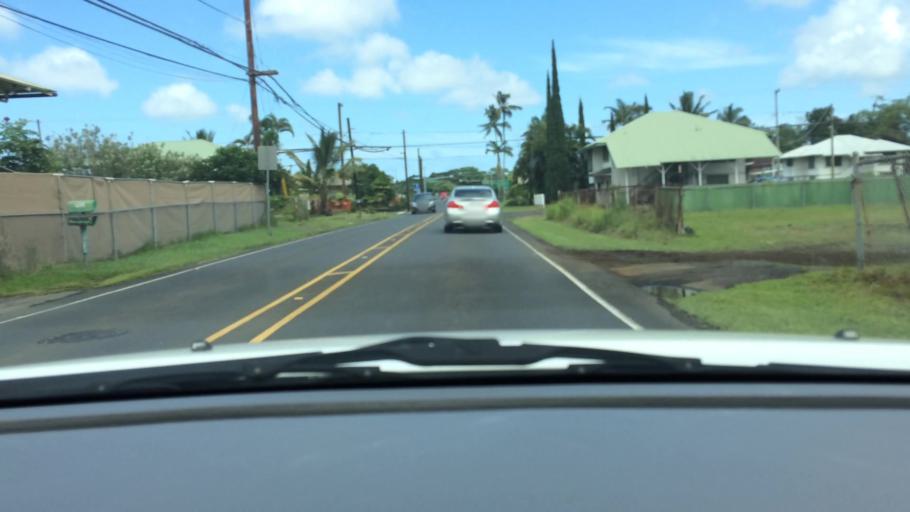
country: US
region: Hawaii
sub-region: Hawaii County
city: Hilo
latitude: 19.7117
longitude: -155.0666
